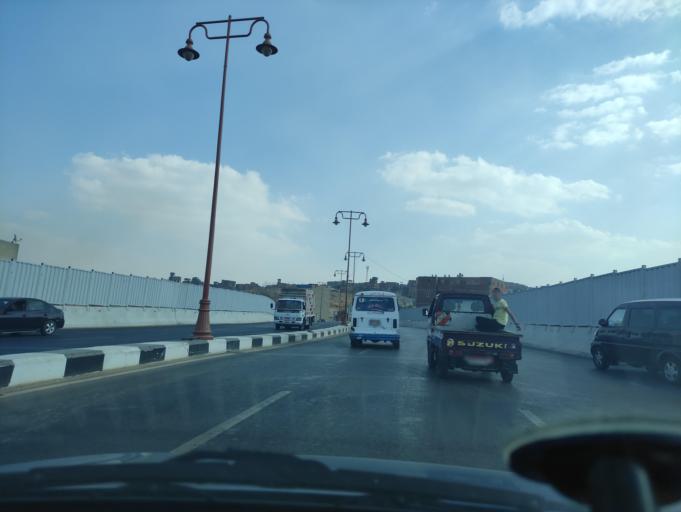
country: EG
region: Muhafazat al Qahirah
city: Cairo
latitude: 30.0490
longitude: 31.2866
